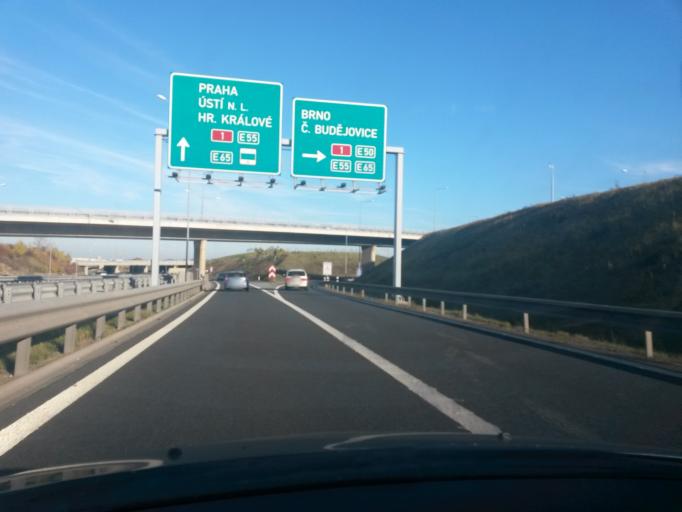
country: CZ
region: Central Bohemia
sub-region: Okres Praha-Vychod
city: Ricany
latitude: 49.9790
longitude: 14.6017
